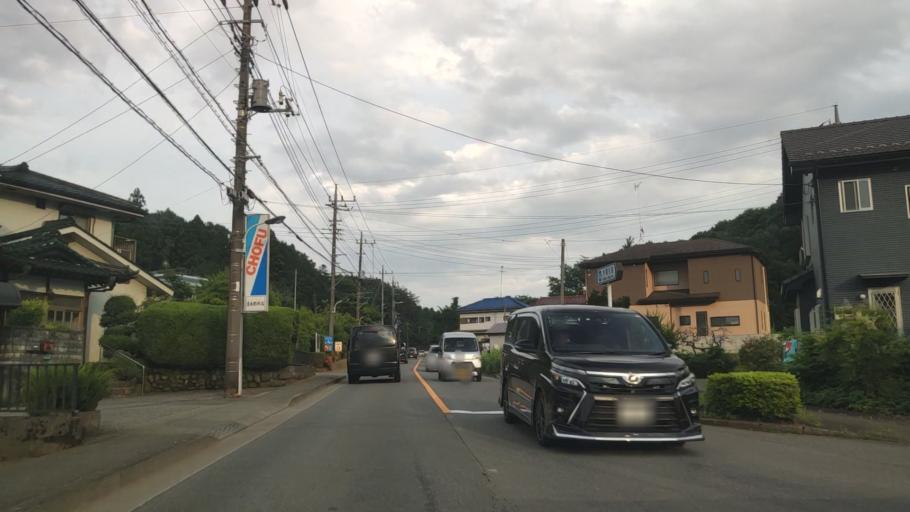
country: JP
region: Saitama
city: Hanno
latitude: 35.8201
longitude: 139.2925
